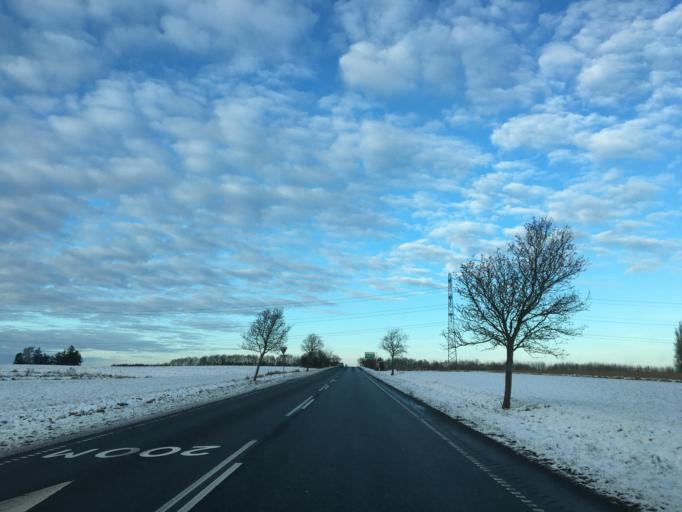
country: DK
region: Zealand
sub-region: Koge Kommune
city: Borup
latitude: 55.4532
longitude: 11.9856
